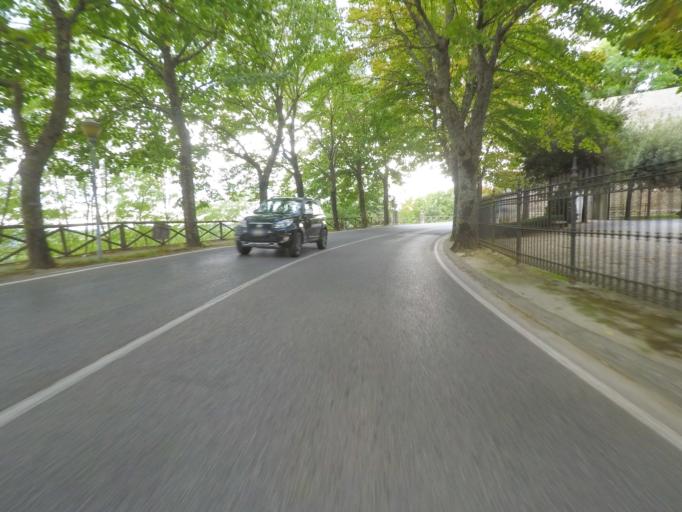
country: IT
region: Tuscany
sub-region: Provincia di Siena
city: Montepulciano
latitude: 43.0974
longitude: 11.7866
